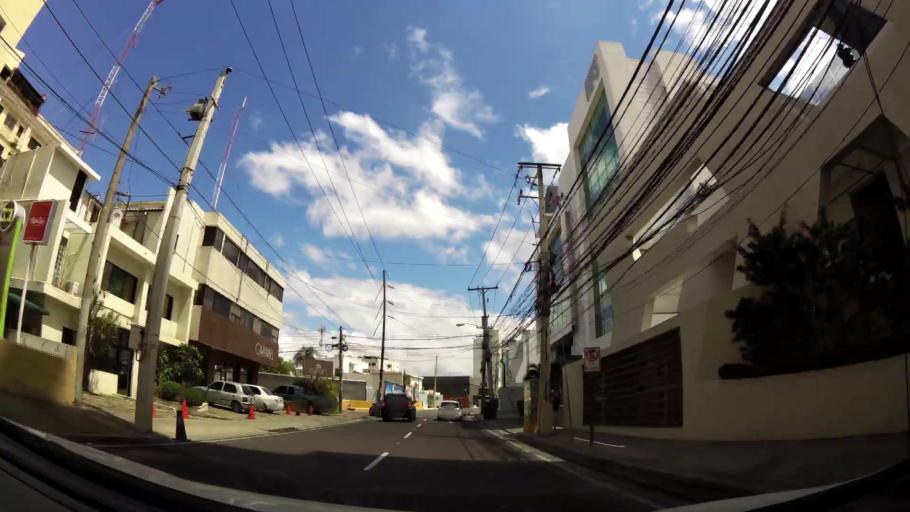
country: DO
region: Nacional
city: La Julia
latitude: 18.4752
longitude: -69.9349
